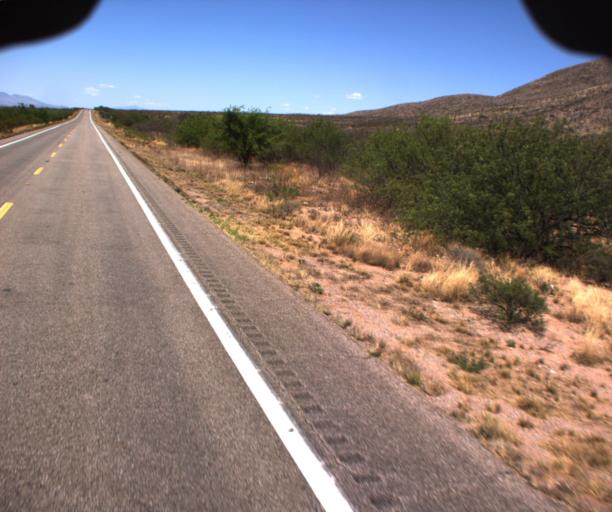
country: US
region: Arizona
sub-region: Cochise County
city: Tombstone
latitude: 31.5811
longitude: -110.0341
